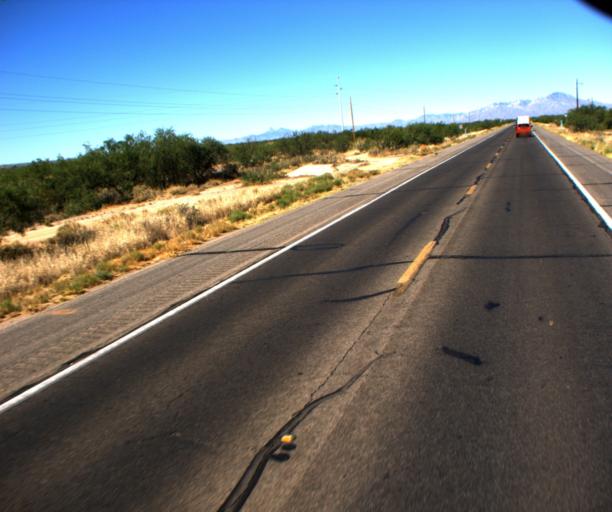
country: US
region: Arizona
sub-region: Pima County
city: Three Points
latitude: 32.1051
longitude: -111.2424
